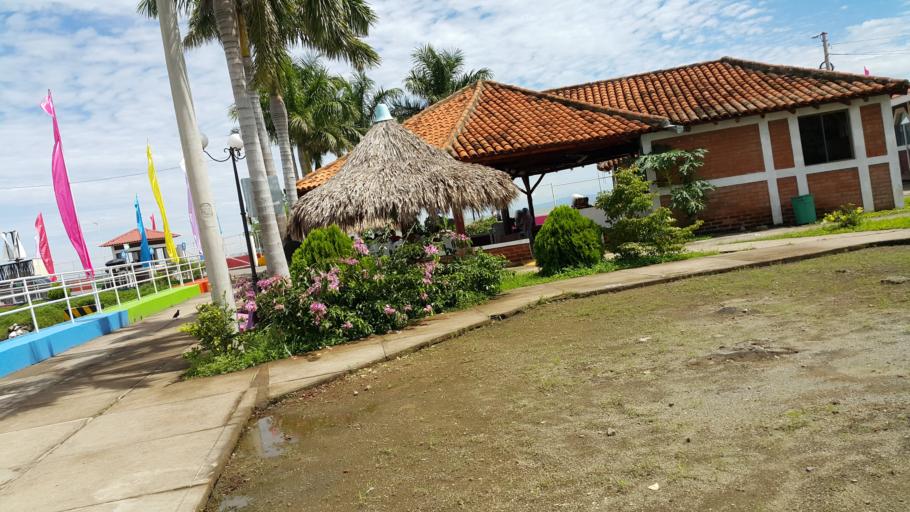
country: NI
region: Rivas
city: San Jorge
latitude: 11.4608
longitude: -85.7901
